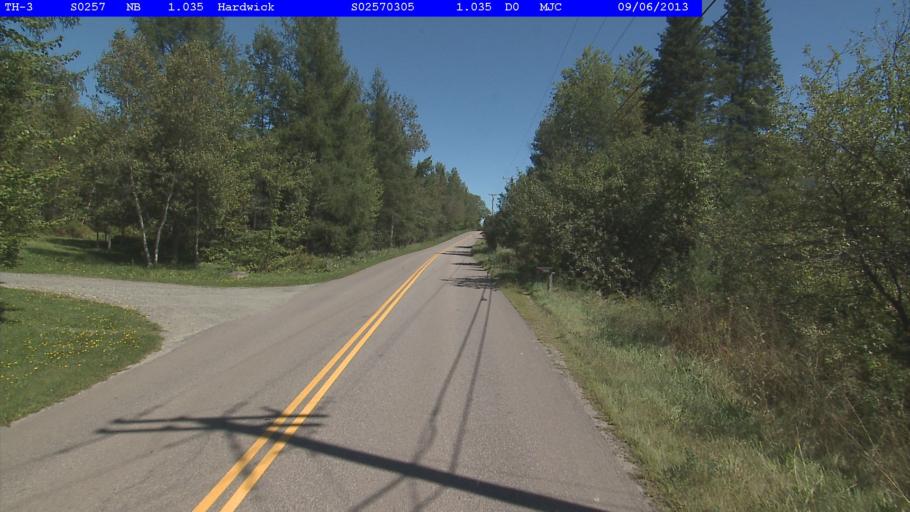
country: US
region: Vermont
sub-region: Caledonia County
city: Hardwick
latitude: 44.5080
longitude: -72.3483
